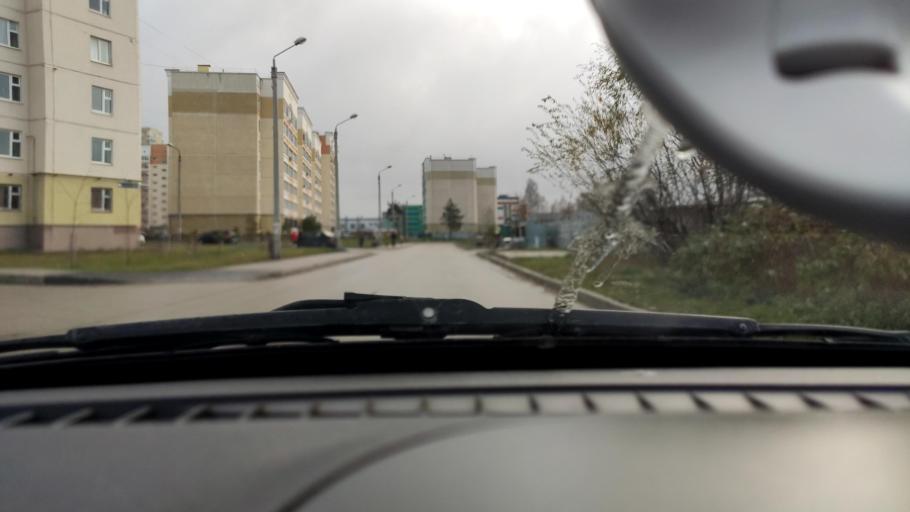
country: RU
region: Perm
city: Kondratovo
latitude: 58.0346
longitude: 56.1349
